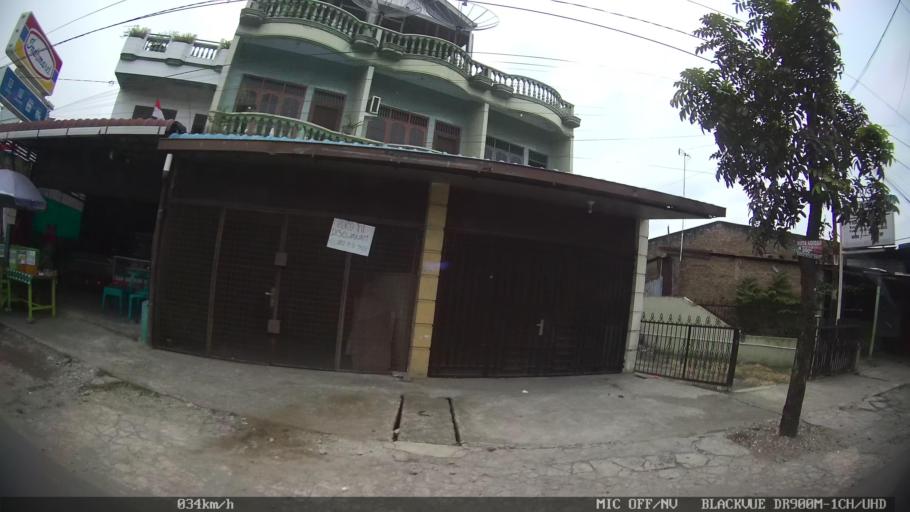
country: ID
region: North Sumatra
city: Medan
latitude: 3.5759
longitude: 98.7264
